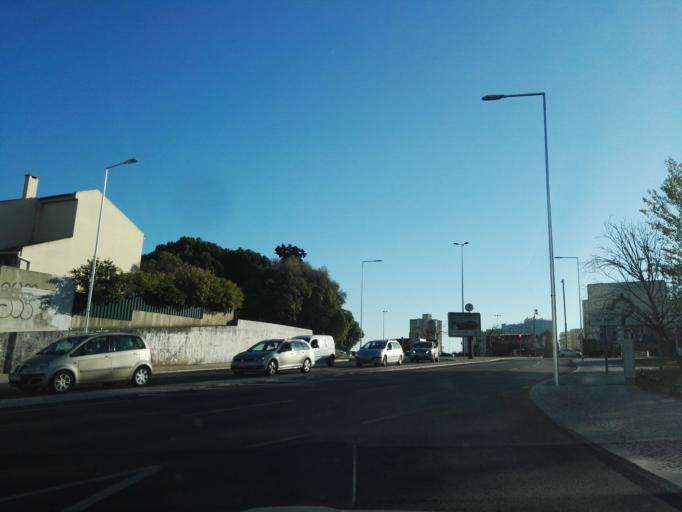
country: PT
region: Lisbon
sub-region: Loures
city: Moscavide
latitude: 38.7623
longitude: -9.1204
